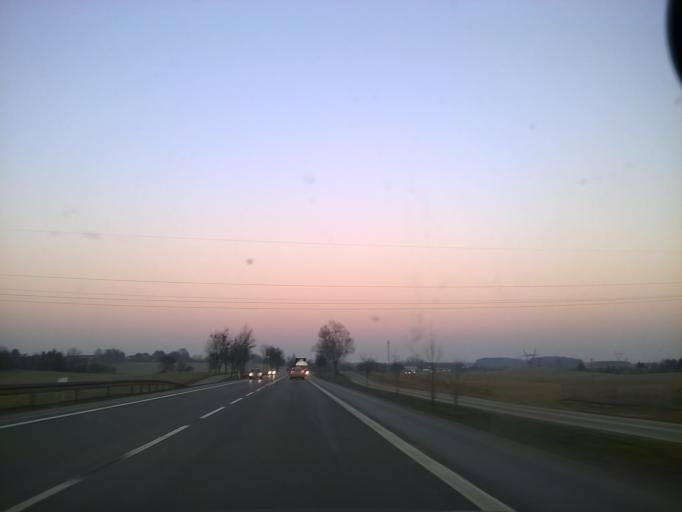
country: PL
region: Warmian-Masurian Voivodeship
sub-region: Powiat olsztynski
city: Olsztyn
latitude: 53.7851
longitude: 20.5774
